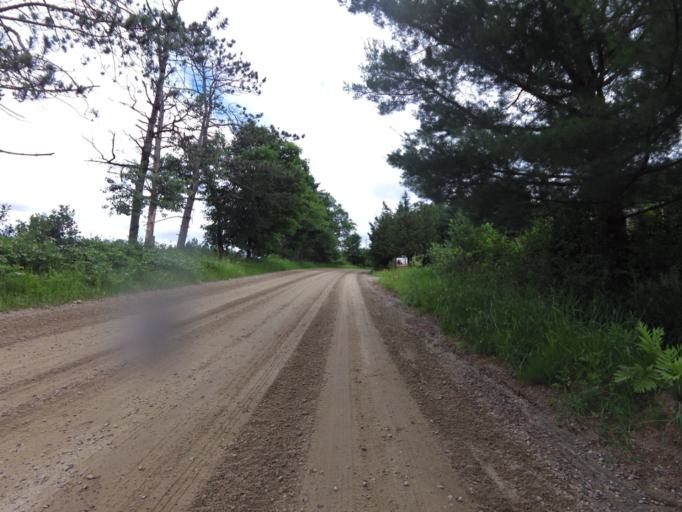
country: CA
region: Quebec
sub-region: Laurentides
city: Mont-Tremblant
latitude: 45.9401
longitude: -74.6502
